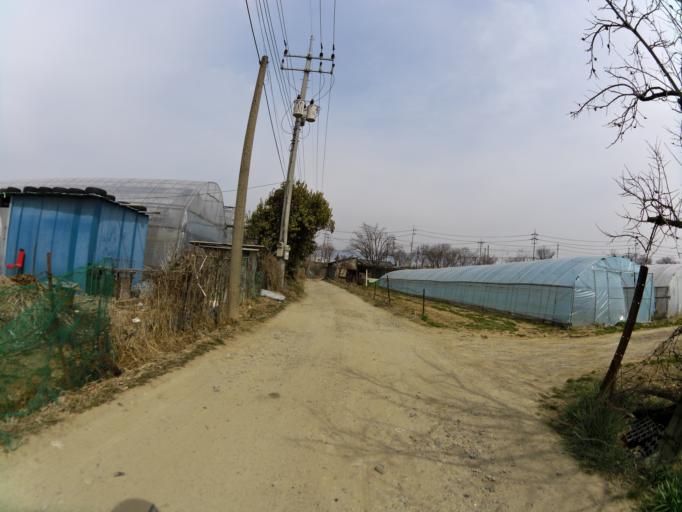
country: KR
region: Gyeongsangbuk-do
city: Gyeongsan-si
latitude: 35.8590
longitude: 128.7161
